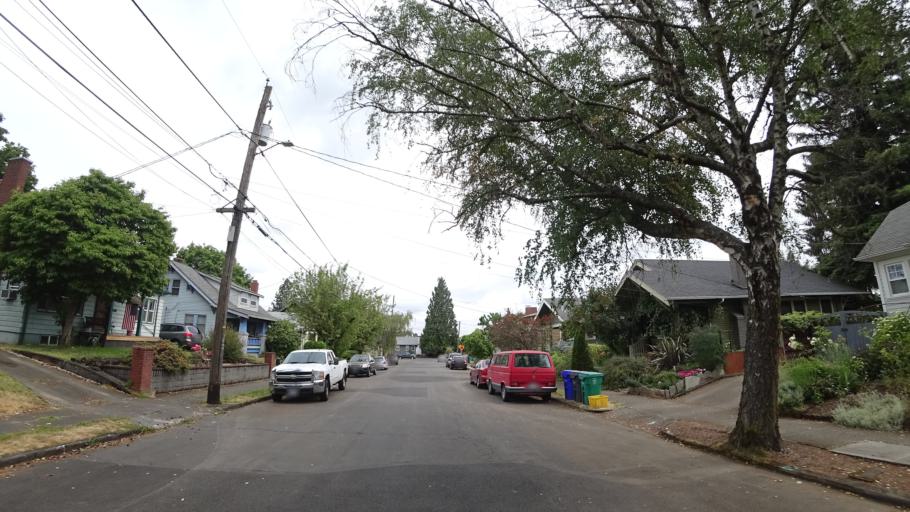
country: US
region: Oregon
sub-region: Multnomah County
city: Portland
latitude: 45.5726
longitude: -122.6777
